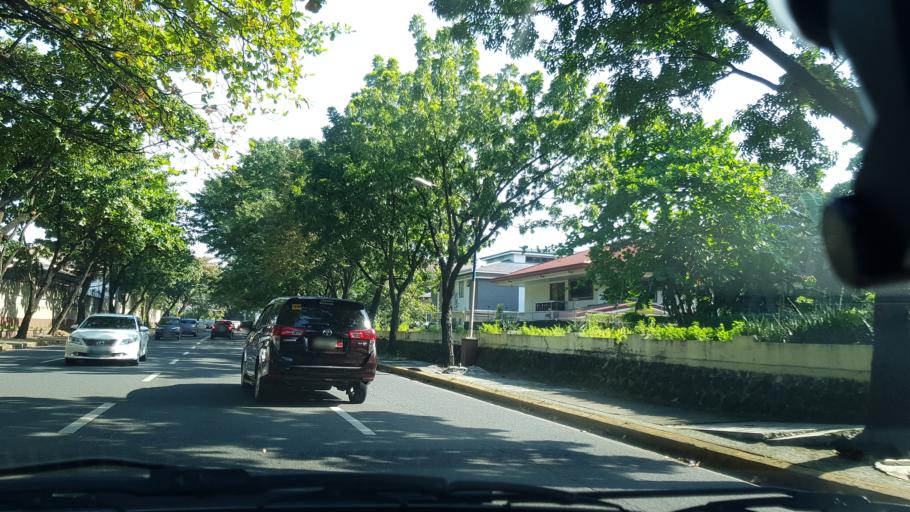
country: PH
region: Metro Manila
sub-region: Pasig
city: Pasig City
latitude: 14.5809
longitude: 121.0707
